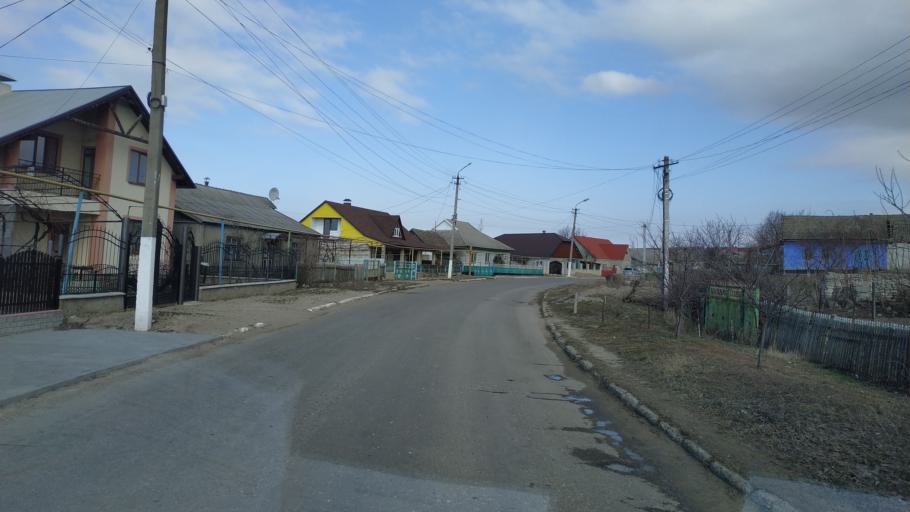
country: MD
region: Causeni
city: Causeni
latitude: 46.6438
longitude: 29.3870
